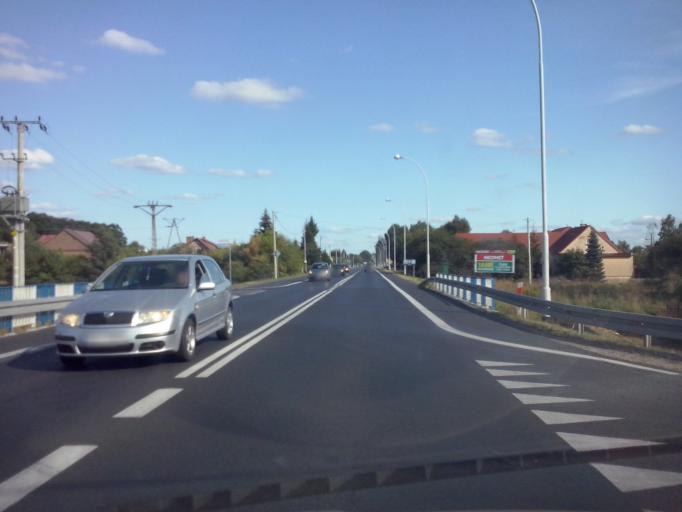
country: PL
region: Subcarpathian Voivodeship
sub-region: Powiat nizanski
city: Nisko
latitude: 50.5286
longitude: 22.1121
